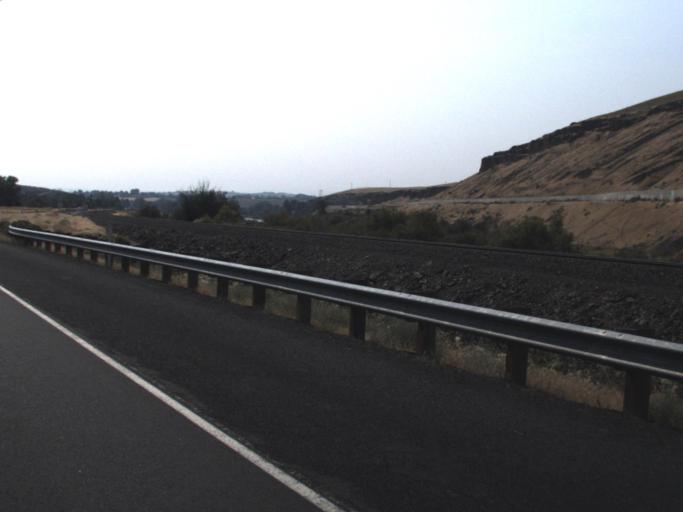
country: US
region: Washington
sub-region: Yakima County
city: Selah
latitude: 46.7141
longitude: -120.4632
